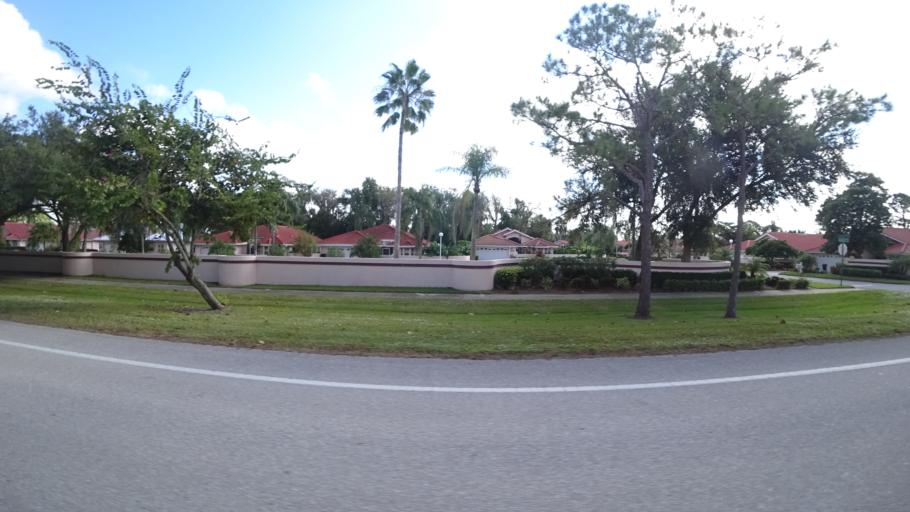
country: US
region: Florida
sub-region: Sarasota County
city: Desoto Lakes
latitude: 27.3962
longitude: -82.4871
